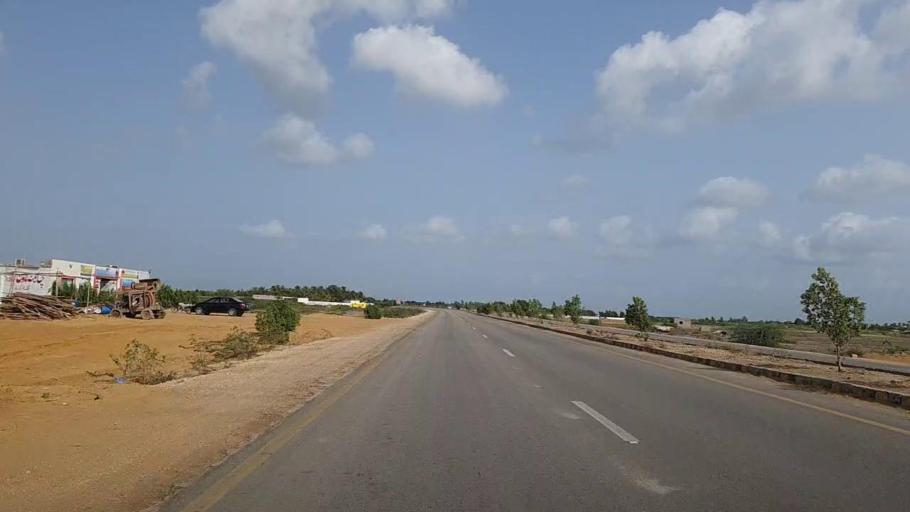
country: PK
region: Sindh
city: Gharo
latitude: 24.7330
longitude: 67.6025
